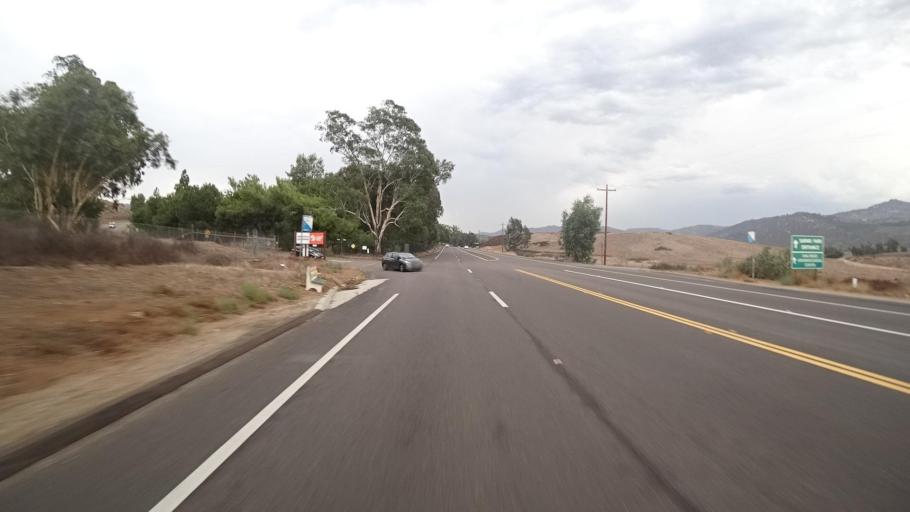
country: US
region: California
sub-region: San Diego County
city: San Pasqual
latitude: 33.0959
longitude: -117.0090
